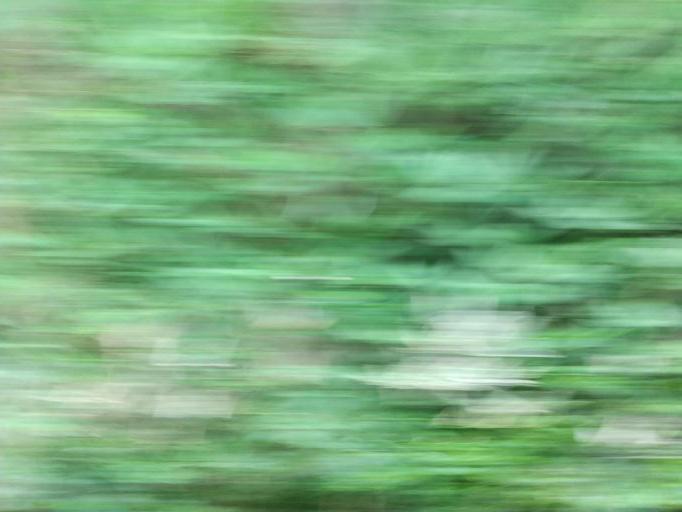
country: JP
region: Miyagi
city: Sendai
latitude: 38.2316
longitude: 140.7289
